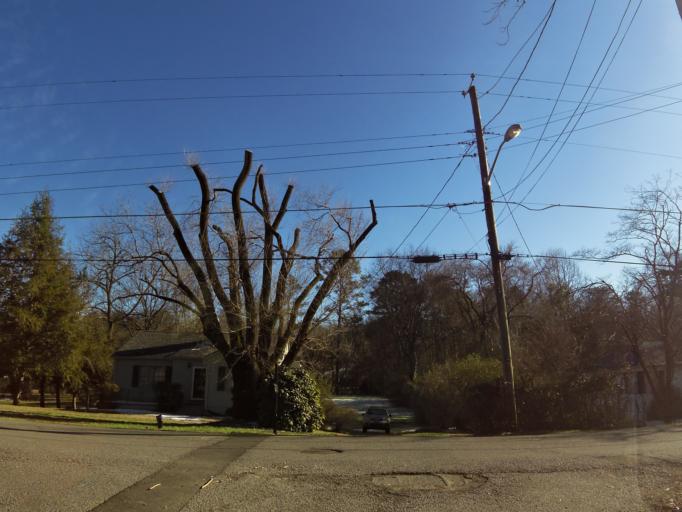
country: US
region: Tennessee
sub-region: Knox County
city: Knoxville
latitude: 35.9111
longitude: -84.0017
